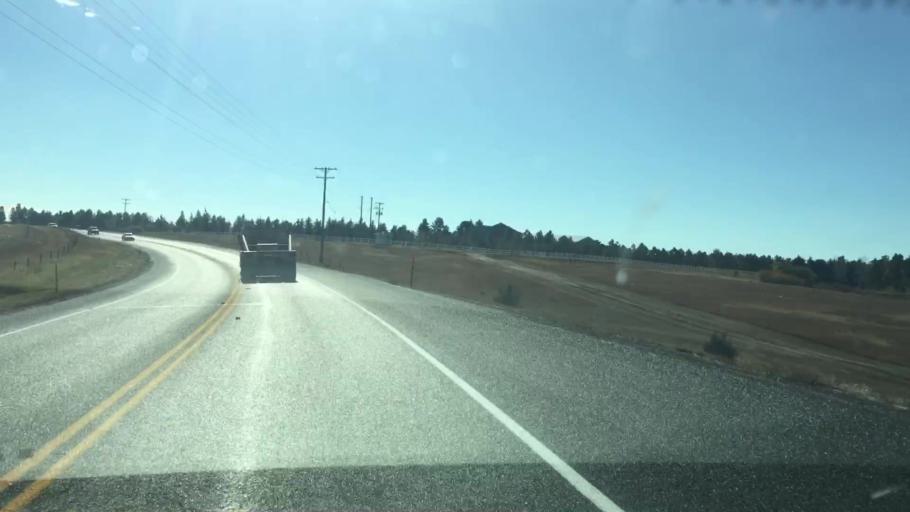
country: US
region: Colorado
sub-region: Elbert County
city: Ponderosa Park
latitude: 39.3633
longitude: -104.6720
